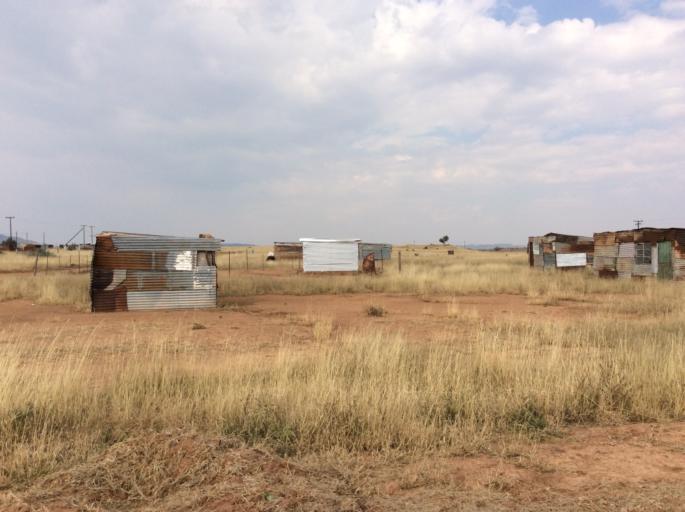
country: LS
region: Mafeteng
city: Mafeteng
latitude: -29.9860
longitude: 27.0000
